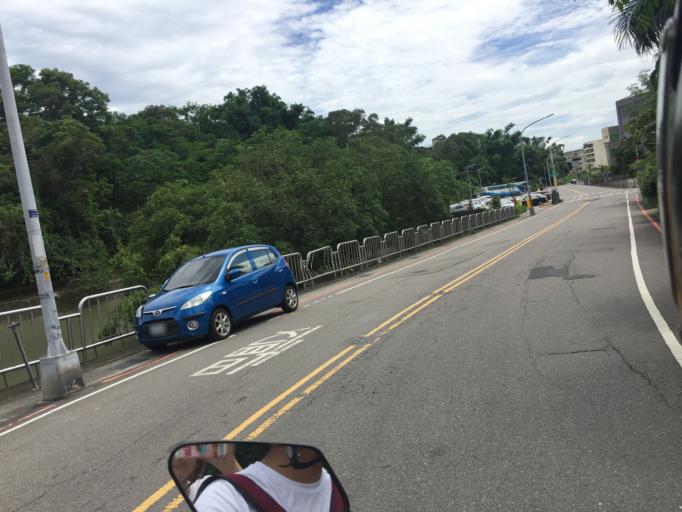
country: TW
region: Taiwan
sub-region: Taichung City
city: Taichung
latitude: 24.0614
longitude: 120.7028
